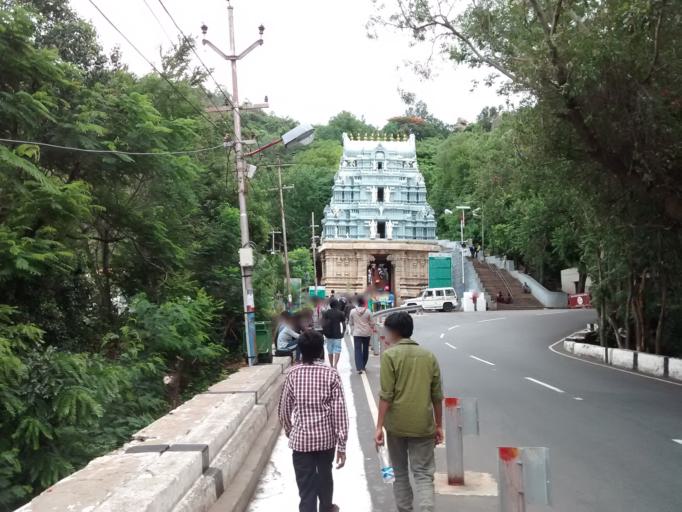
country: IN
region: Andhra Pradesh
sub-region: Chittoor
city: Tirumala
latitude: 13.6661
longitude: 79.3551
